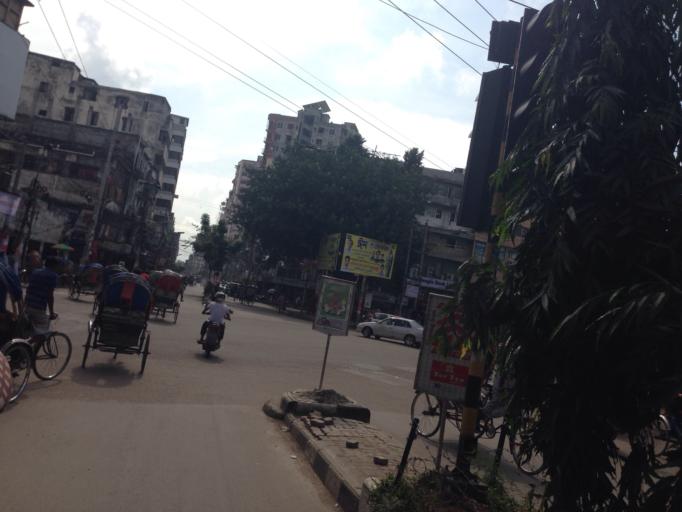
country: BD
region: Dhaka
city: Azimpur
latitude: 23.7393
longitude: 90.3888
